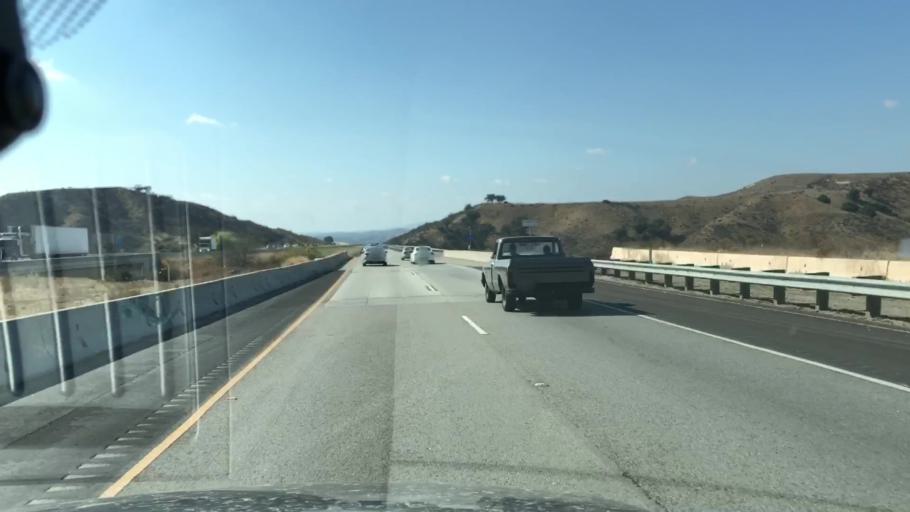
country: US
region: California
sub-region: Ventura County
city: Simi Valley
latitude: 34.2910
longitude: -118.8097
